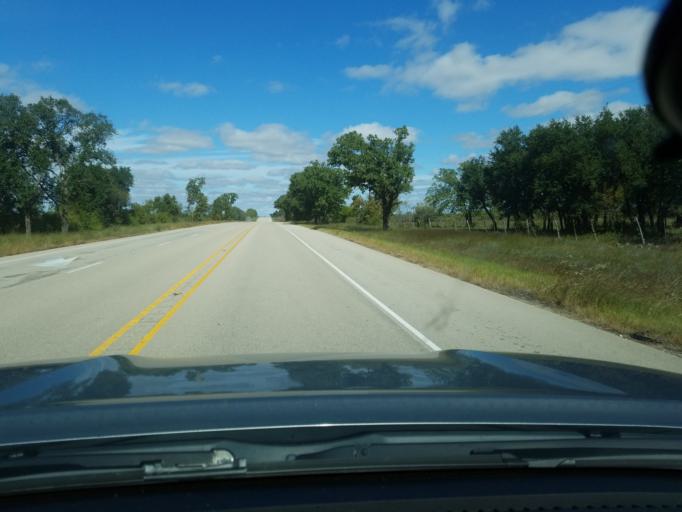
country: US
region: Texas
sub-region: Hamilton County
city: Hamilton
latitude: 31.5620
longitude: -98.1590
